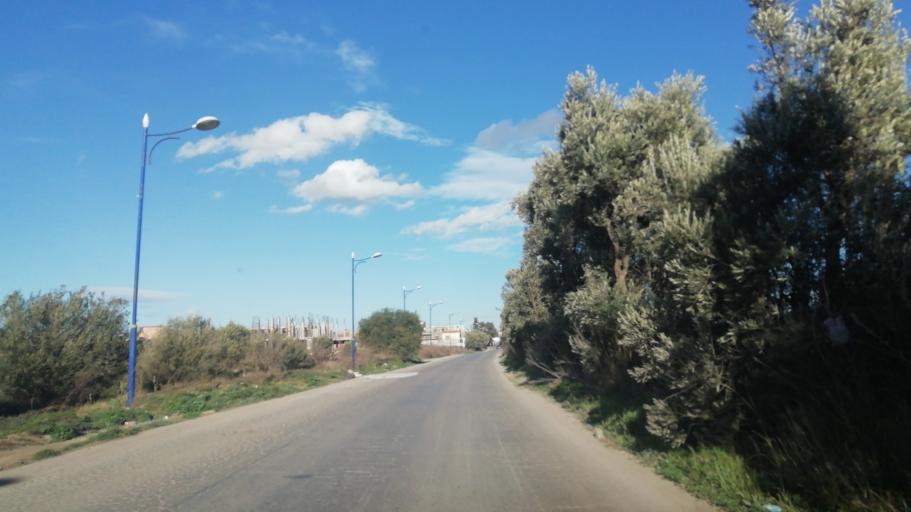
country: DZ
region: Oran
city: Sidi ech Chahmi
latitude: 35.6527
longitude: -0.5293
